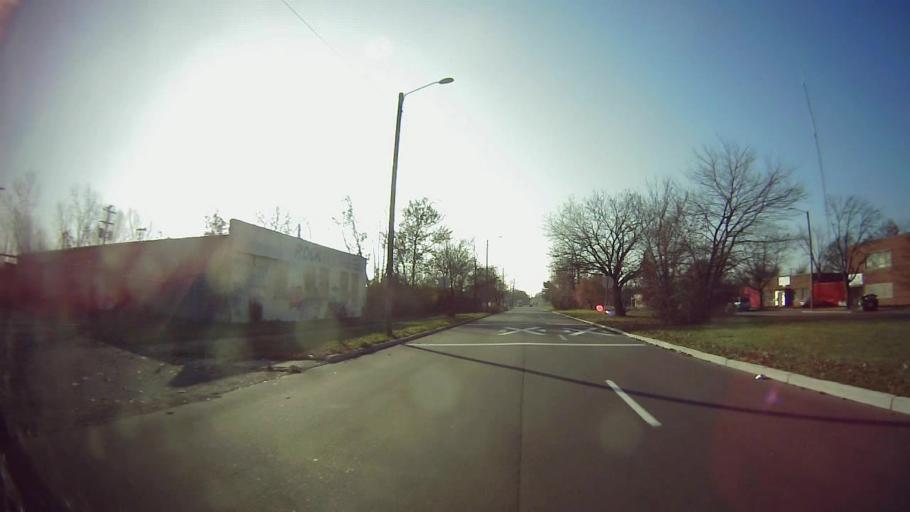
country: US
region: Michigan
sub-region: Wayne County
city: Dearborn
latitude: 42.3682
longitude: -83.1513
